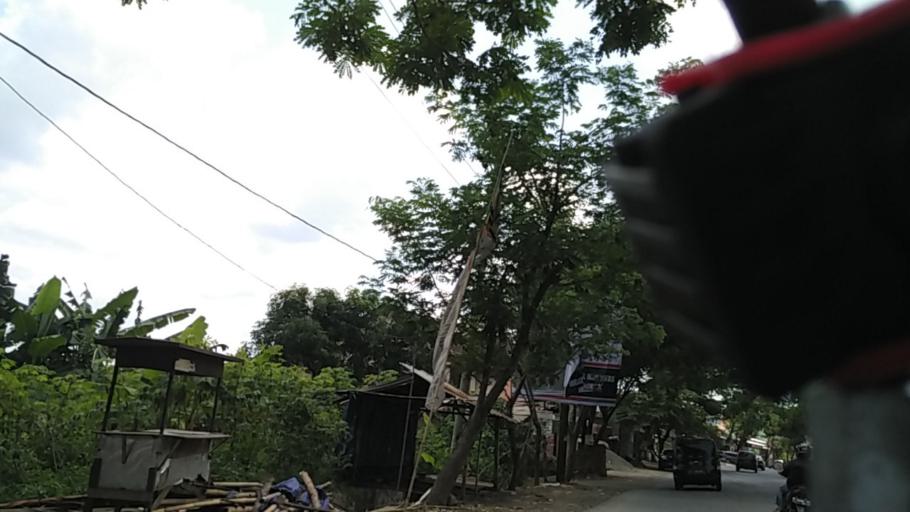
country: ID
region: Central Java
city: Semarang
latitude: -7.0170
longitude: 110.3385
